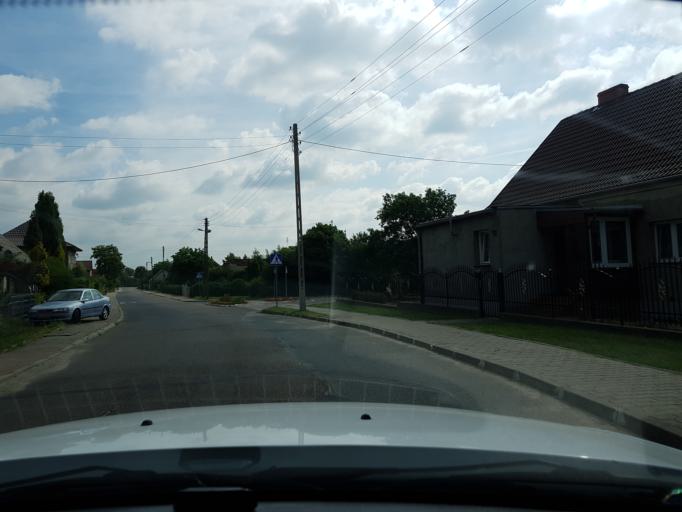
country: PL
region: West Pomeranian Voivodeship
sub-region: Powiat gryfinski
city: Banie
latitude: 53.1278
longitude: 14.6077
